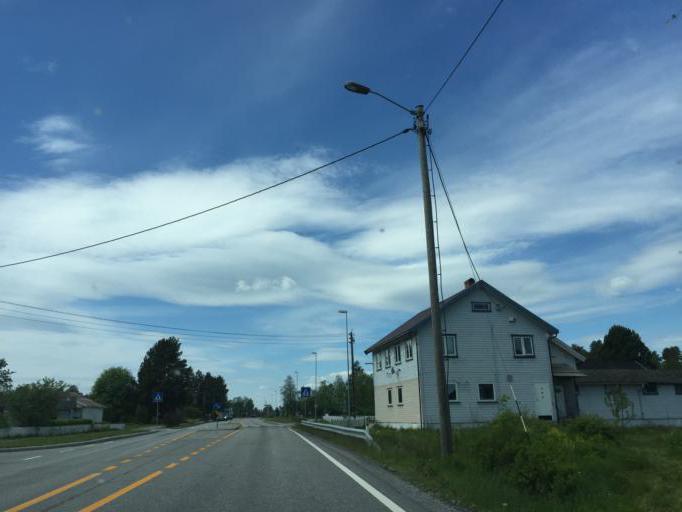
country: NO
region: Akershus
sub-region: Nes
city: Arnes
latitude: 60.1795
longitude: 11.5164
